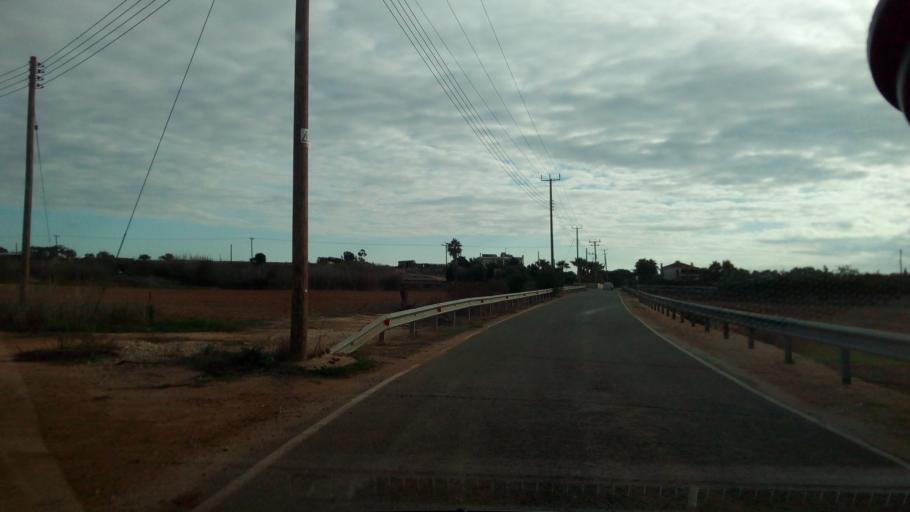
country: CY
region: Ammochostos
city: Liopetri
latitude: 35.0432
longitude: 33.8874
